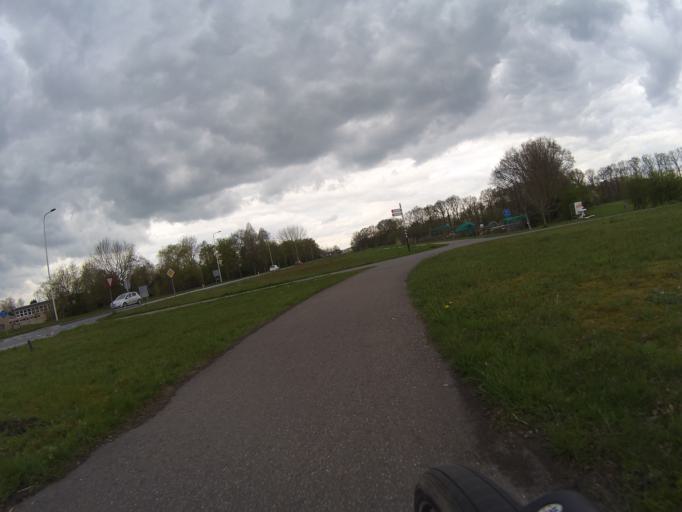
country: NL
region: Gelderland
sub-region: Gemeente Nijkerk
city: Nijkerk
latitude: 52.2317
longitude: 5.4933
